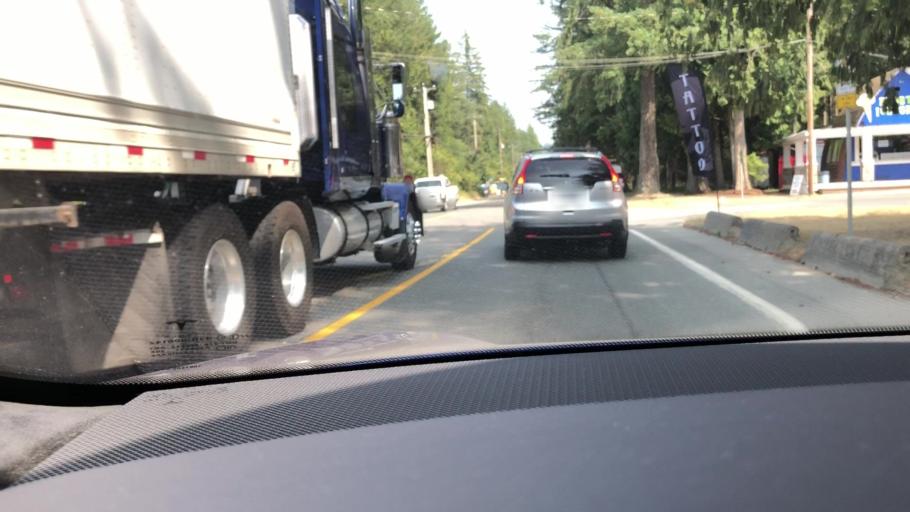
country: CA
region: British Columbia
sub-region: Fraser Valley Regional District
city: Chilliwack
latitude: 49.0749
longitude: -121.9741
